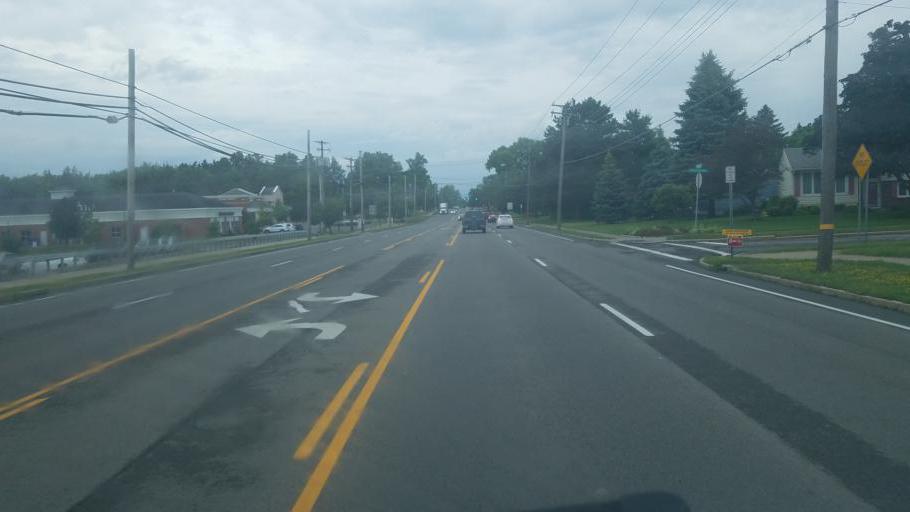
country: US
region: New York
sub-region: Niagara County
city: South Lockport
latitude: 43.1527
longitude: -78.6968
